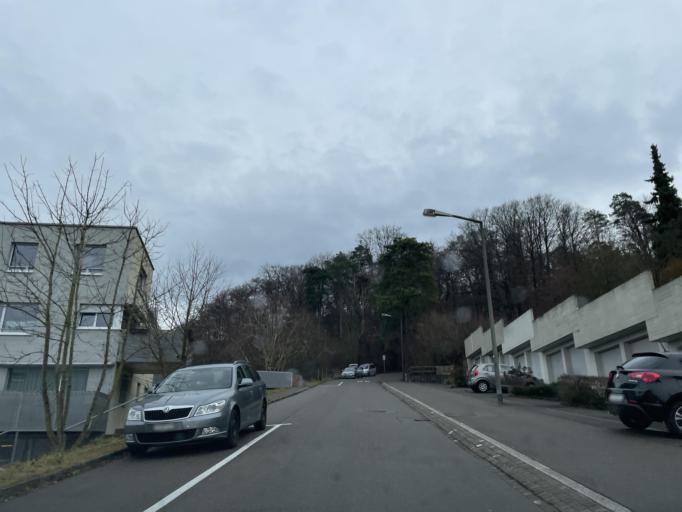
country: CH
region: Zurich
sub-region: Bezirk Winterthur
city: Wuelflingen (Kreis 6) / Lindenplatz
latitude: 47.5058
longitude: 8.6958
